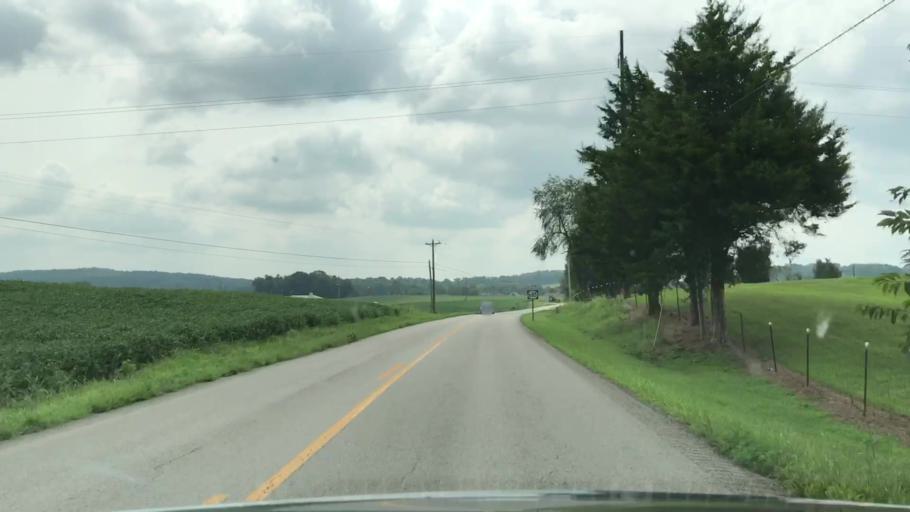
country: US
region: Kentucky
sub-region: Barren County
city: Cave City
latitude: 37.0997
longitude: -85.9759
